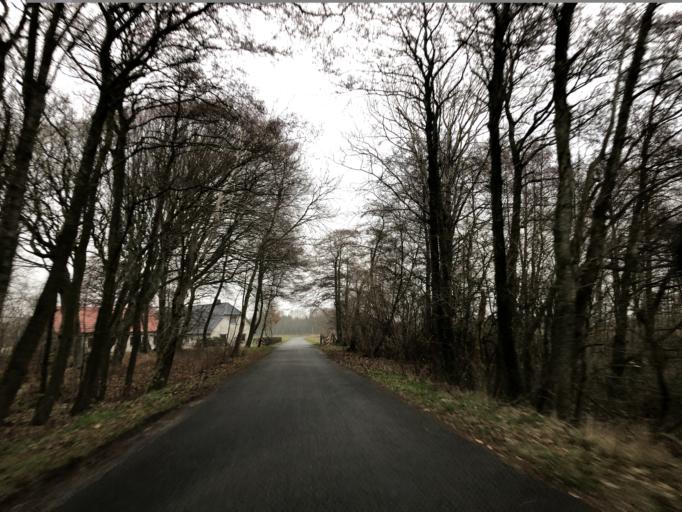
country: DK
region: Central Jutland
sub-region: Holstebro Kommune
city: Ulfborg
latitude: 56.2008
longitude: 8.3138
